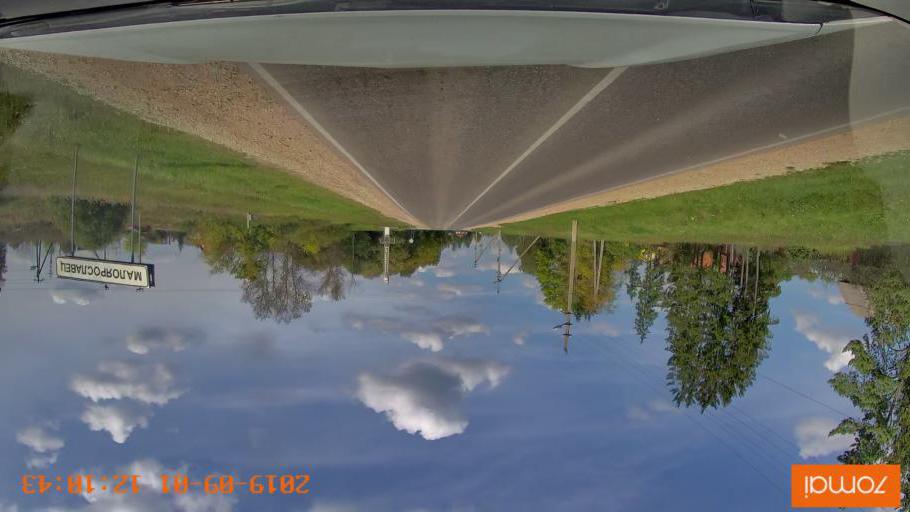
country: RU
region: Kaluga
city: Maloyaroslavets
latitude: 54.9944
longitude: 36.4352
